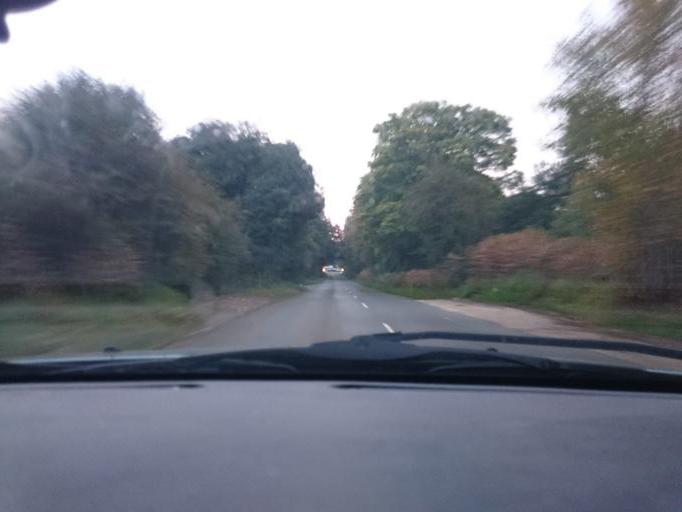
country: GB
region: England
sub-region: Hampshire
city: Lindford
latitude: 51.1264
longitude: -0.8498
